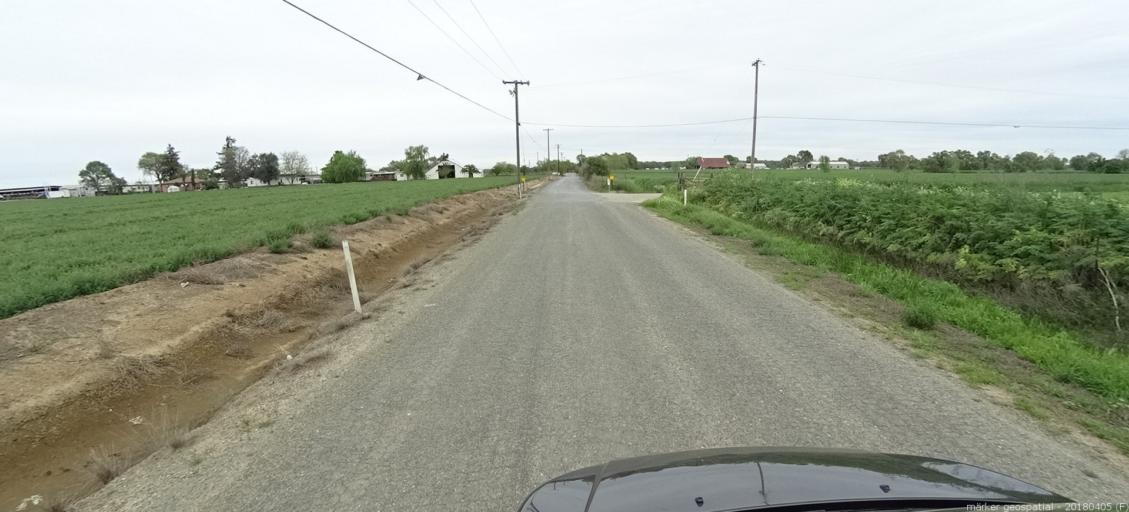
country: US
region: California
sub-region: Sacramento County
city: Elk Grove
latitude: 38.3216
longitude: -121.3974
